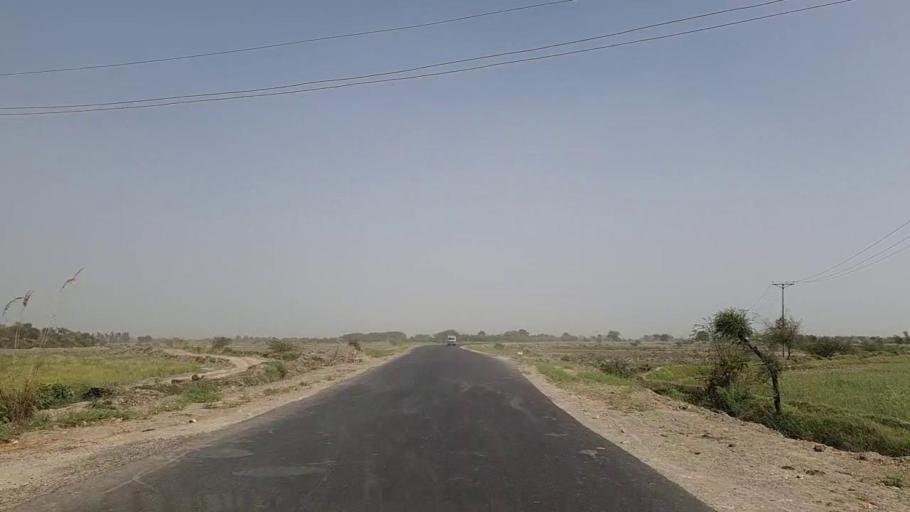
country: PK
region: Sindh
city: Tando Bago
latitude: 24.8095
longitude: 68.9265
